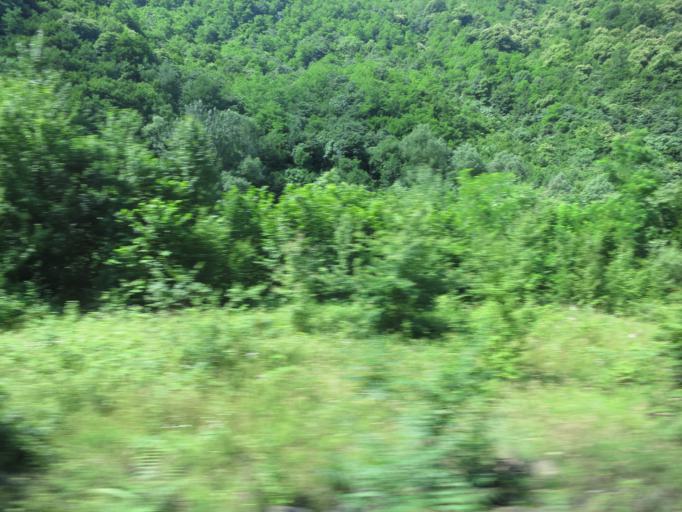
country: GE
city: Shorapani
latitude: 42.0819
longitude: 43.1427
